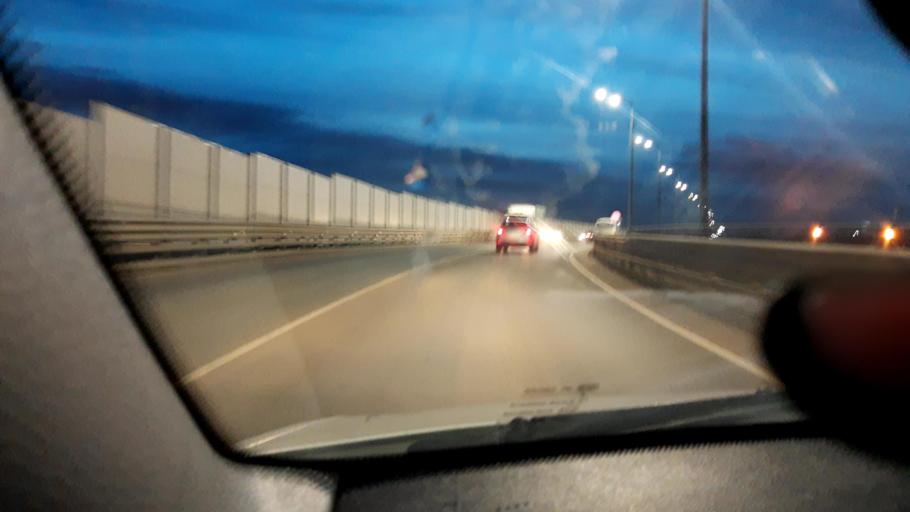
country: RU
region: Bashkortostan
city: Ufa
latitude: 54.8282
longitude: 56.1284
